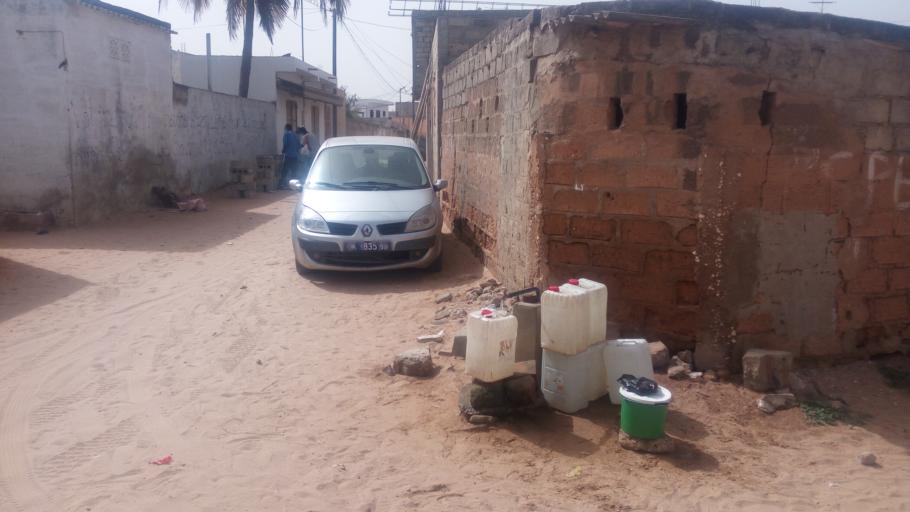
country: SN
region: Dakar
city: Pikine
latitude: 14.7929
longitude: -17.3395
